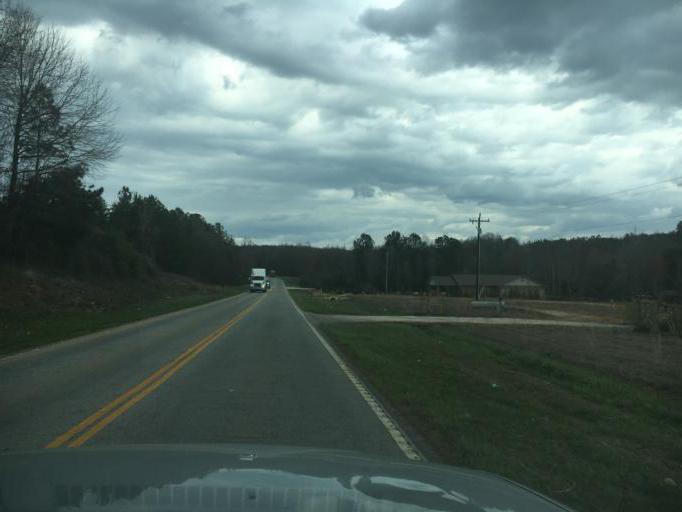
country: US
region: South Carolina
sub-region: Oconee County
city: Walhalla
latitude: 34.7401
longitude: -83.0511
